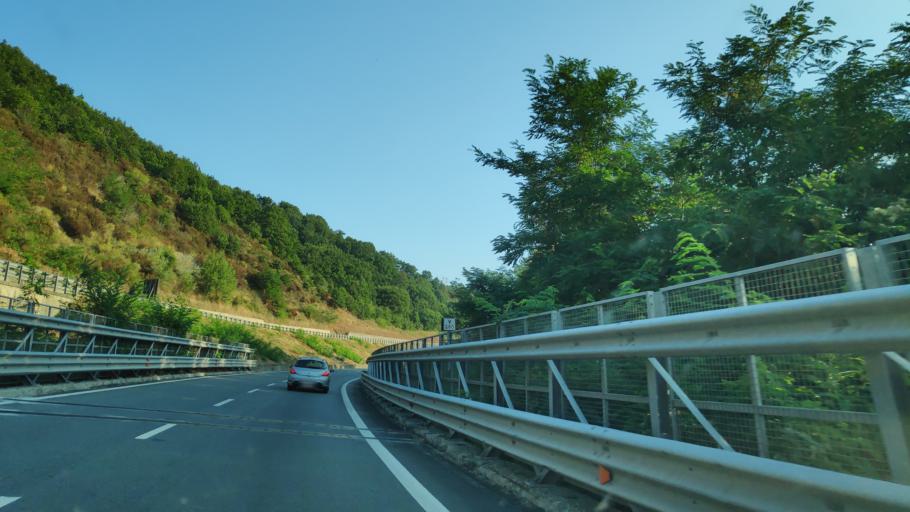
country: IT
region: Calabria
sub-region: Provincia di Cosenza
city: Belsito
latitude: 39.1584
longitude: 16.2871
